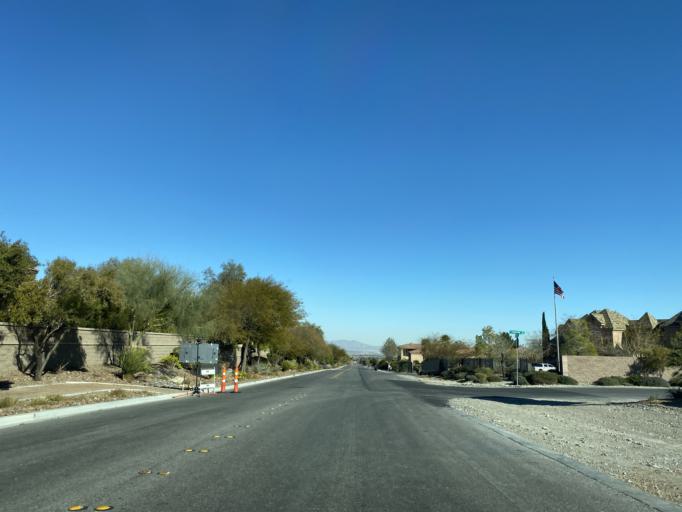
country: US
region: Nevada
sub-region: Clark County
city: Summerlin South
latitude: 36.2957
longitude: -115.3106
